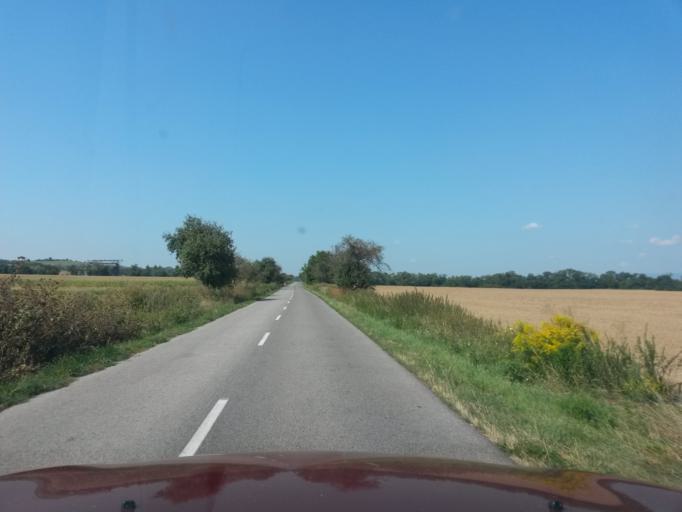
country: HU
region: Borsod-Abauj-Zemplen
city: Gonc
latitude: 48.5345
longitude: 21.1649
